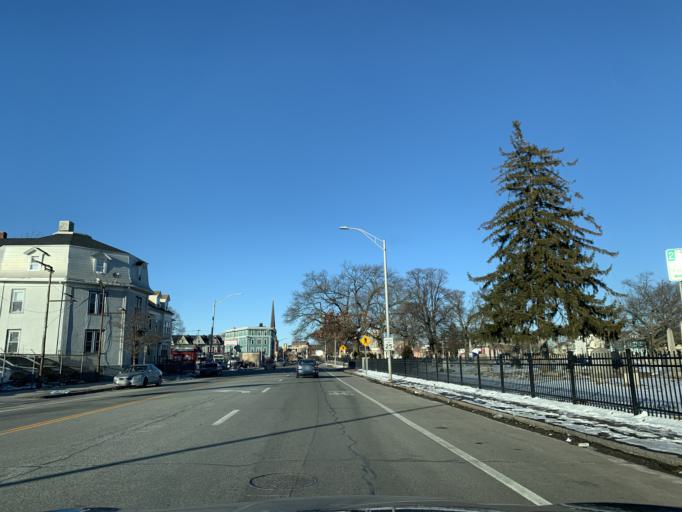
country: US
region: Rhode Island
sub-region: Providence County
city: Providence
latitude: 41.8105
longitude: -71.4236
